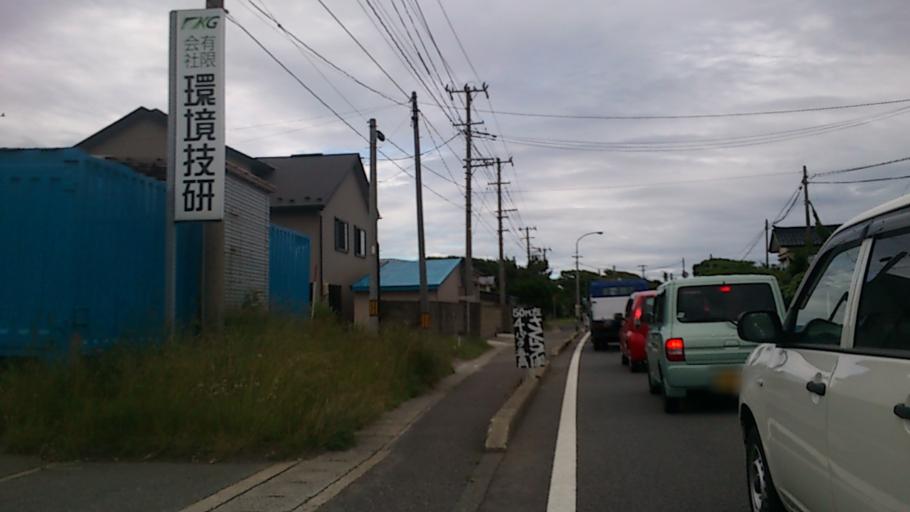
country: JP
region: Akita
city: Akita Shi
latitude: 39.6305
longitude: 140.0655
